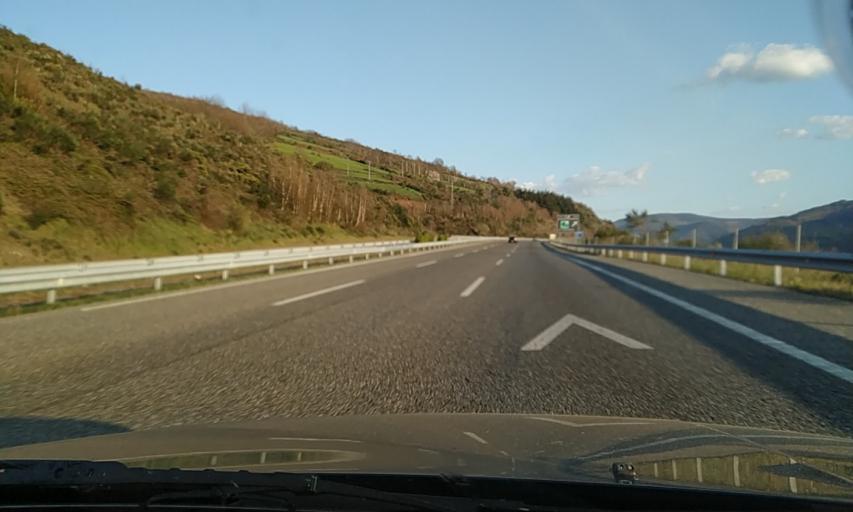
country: ES
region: Galicia
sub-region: Provincia de Lugo
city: San Roman
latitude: 42.7730
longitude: -7.0936
